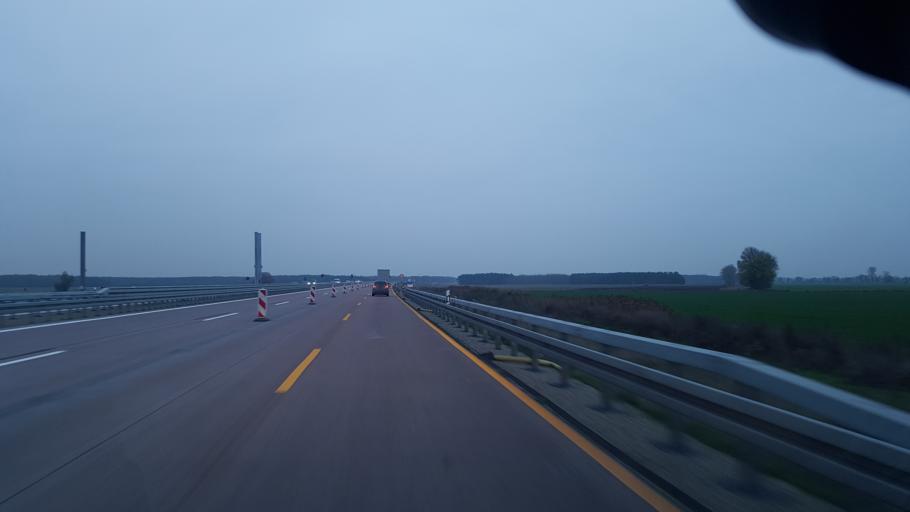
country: DE
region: Brandenburg
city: Kremmen
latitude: 52.7435
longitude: 12.8993
